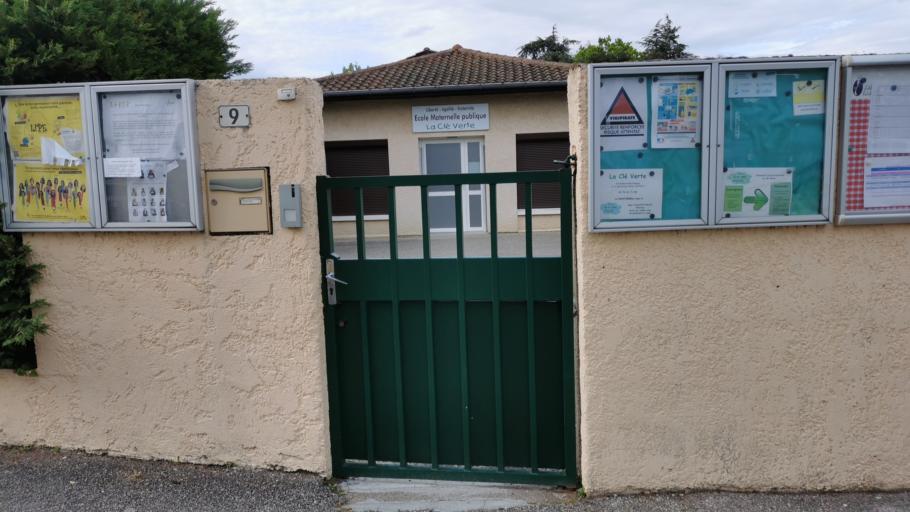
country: FR
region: Rhone-Alpes
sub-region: Departement du Rhone
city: Lentilly
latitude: 45.8202
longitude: 4.6646
